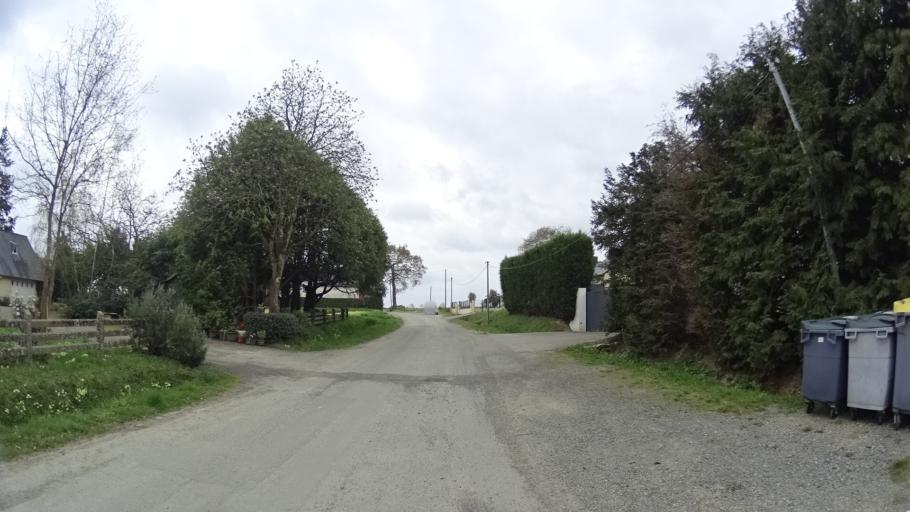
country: FR
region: Brittany
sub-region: Departement d'Ille-et-Vilaine
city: Cintre
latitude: 48.1071
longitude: -1.8641
